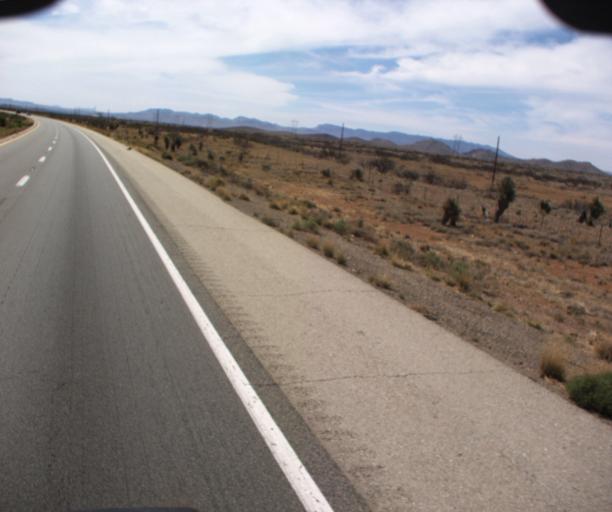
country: US
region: Arizona
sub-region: Cochise County
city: Willcox
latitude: 32.3476
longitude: -109.7457
